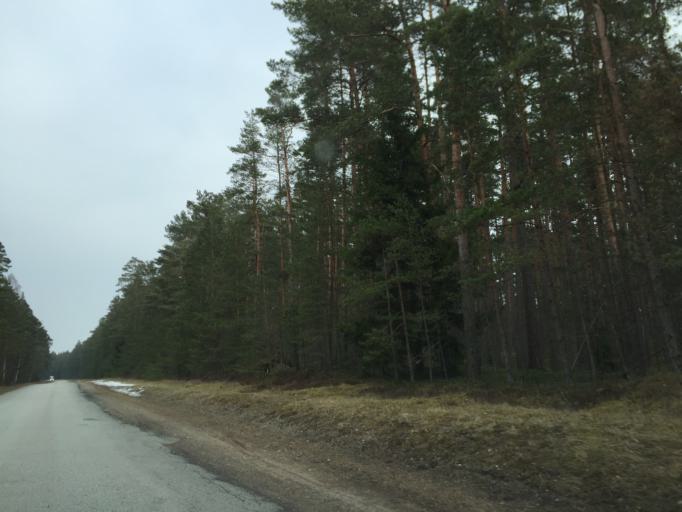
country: LV
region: Salacgrivas
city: Ainazi
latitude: 57.9760
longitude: 24.4129
